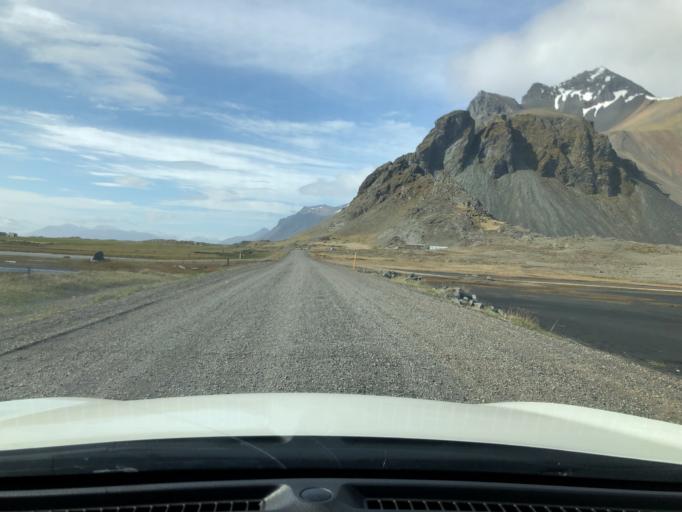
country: IS
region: East
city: Hoefn
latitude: 64.2520
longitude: -14.9890
